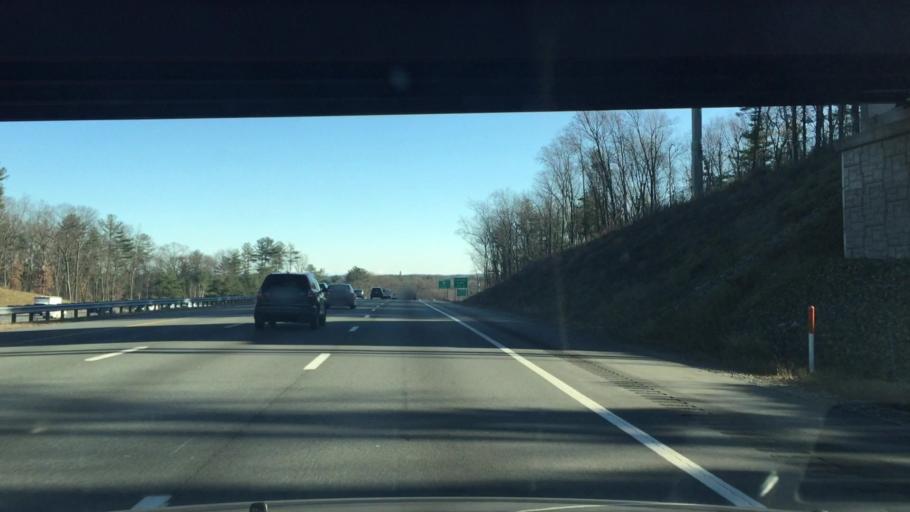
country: US
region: New Hampshire
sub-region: Rockingham County
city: Windham
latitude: 42.7830
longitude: -71.2557
